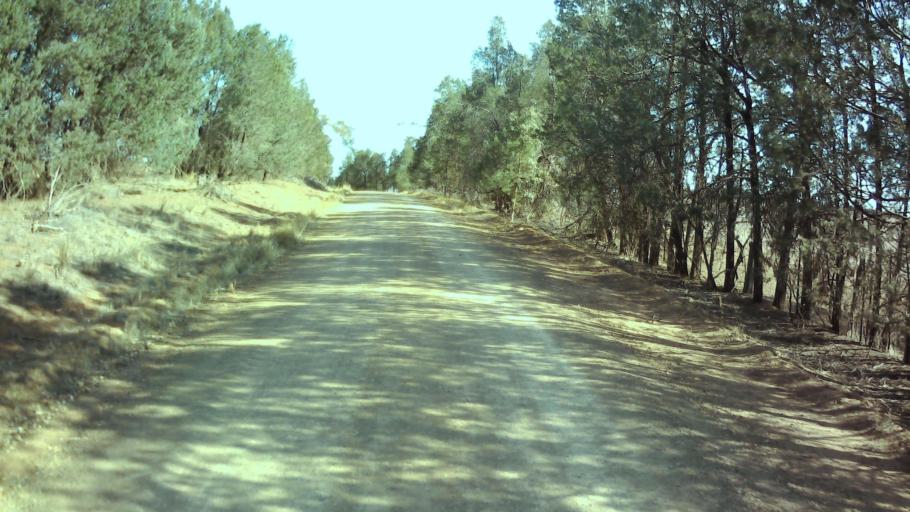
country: AU
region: New South Wales
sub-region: Weddin
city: Grenfell
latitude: -33.7678
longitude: 148.0475
